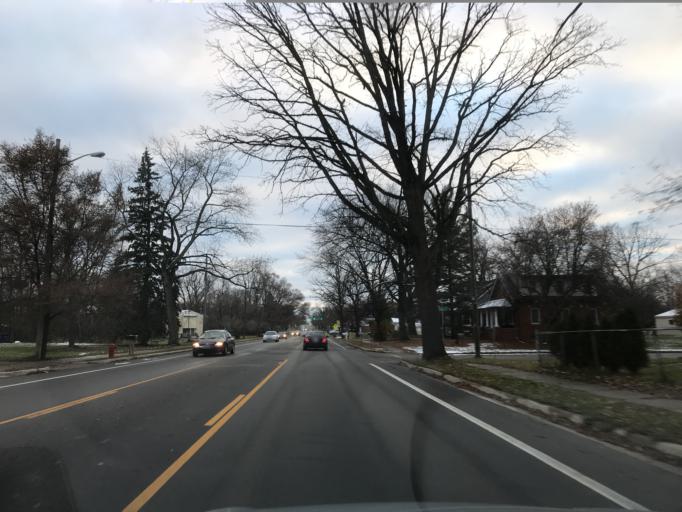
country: US
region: Michigan
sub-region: Washtenaw County
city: Ann Arbor
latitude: 42.2405
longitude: -83.7000
